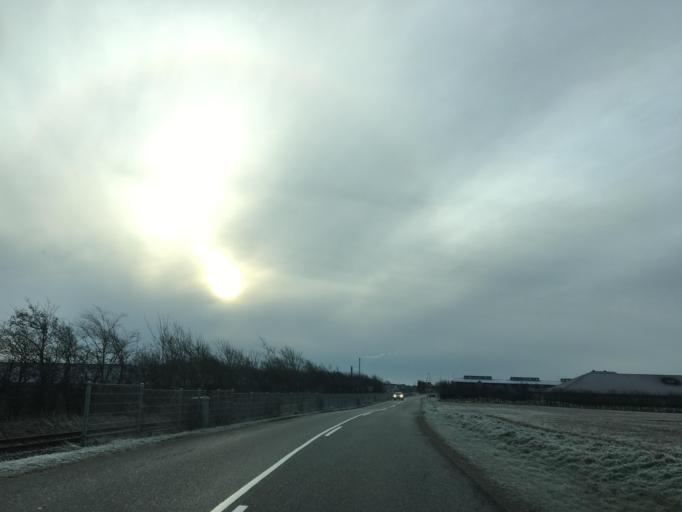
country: DK
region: North Denmark
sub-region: Thisted Kommune
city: Hurup
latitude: 56.7569
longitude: 8.4196
